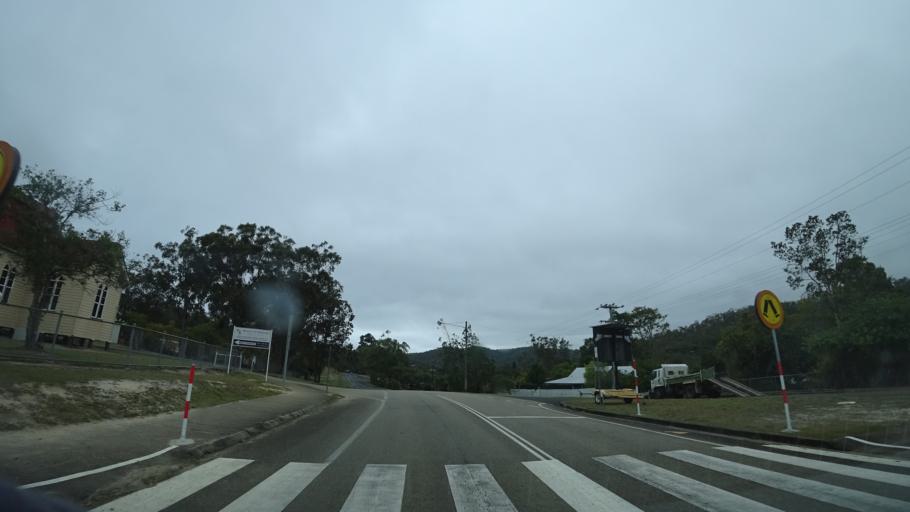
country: AU
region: Queensland
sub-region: Tablelands
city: Atherton
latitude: -17.3796
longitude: 145.3843
